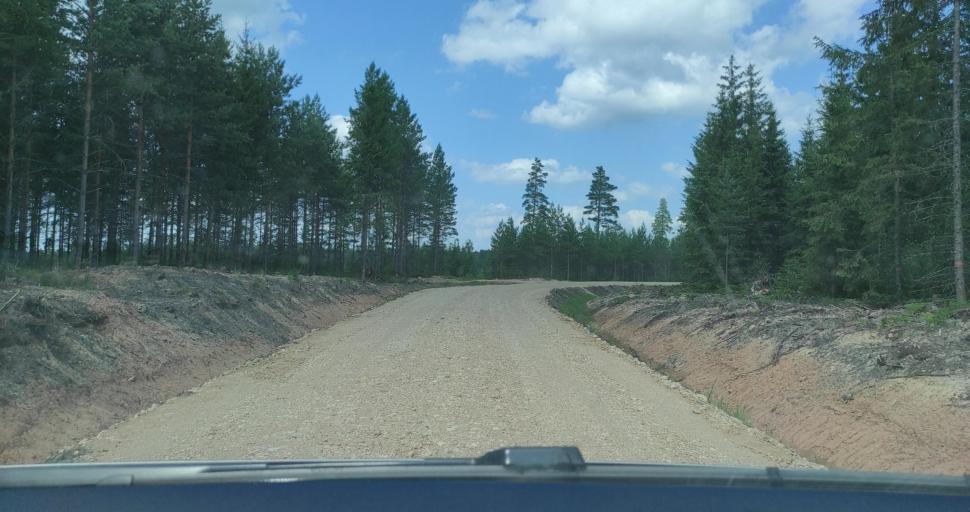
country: LV
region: Kuldigas Rajons
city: Kuldiga
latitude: 57.0589
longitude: 22.1891
